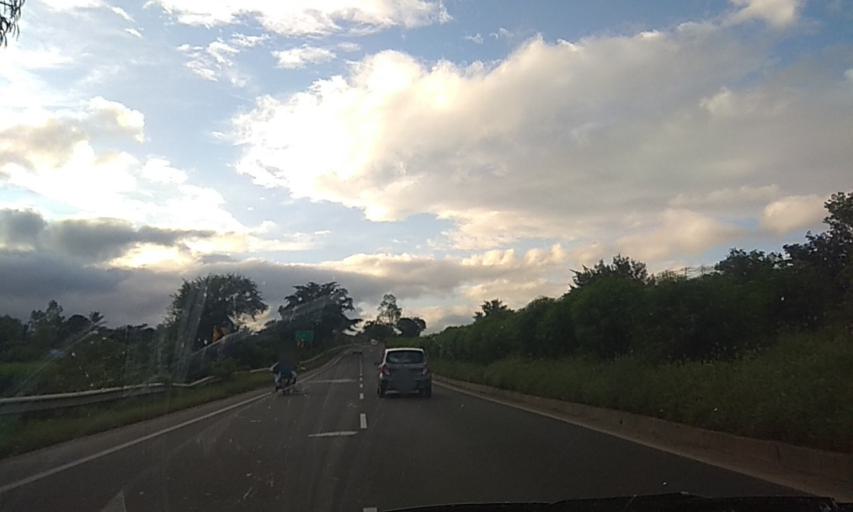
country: IN
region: Maharashtra
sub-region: Satara Division
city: Satara
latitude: 17.5966
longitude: 74.0386
